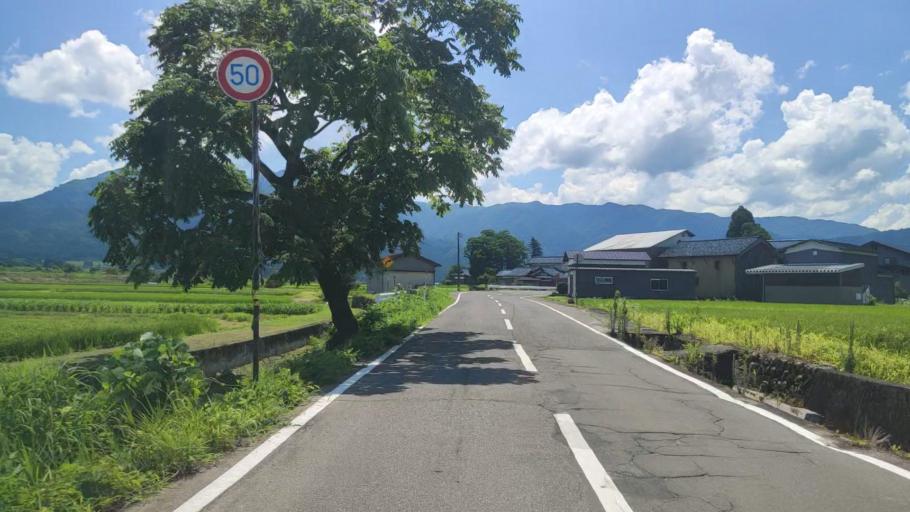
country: JP
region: Fukui
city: Ono
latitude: 35.9696
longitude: 136.5270
